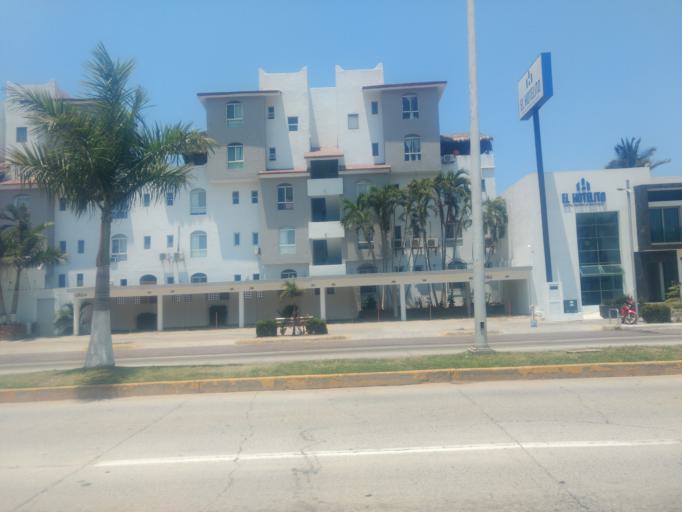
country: MX
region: Colima
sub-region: Manzanillo
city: Manzanillo
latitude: 19.0939
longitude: -104.3176
